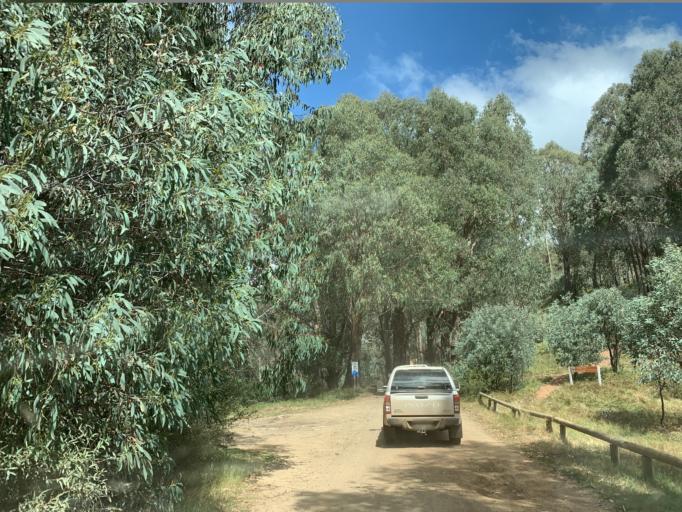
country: AU
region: Victoria
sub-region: Mansfield
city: Mansfield
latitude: -37.1061
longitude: 146.5360
